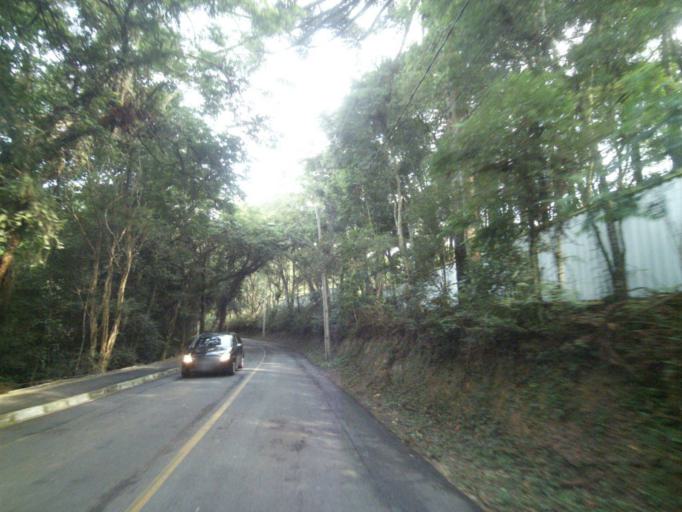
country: BR
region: Parana
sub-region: Curitiba
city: Curitiba
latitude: -25.4219
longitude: -49.3128
